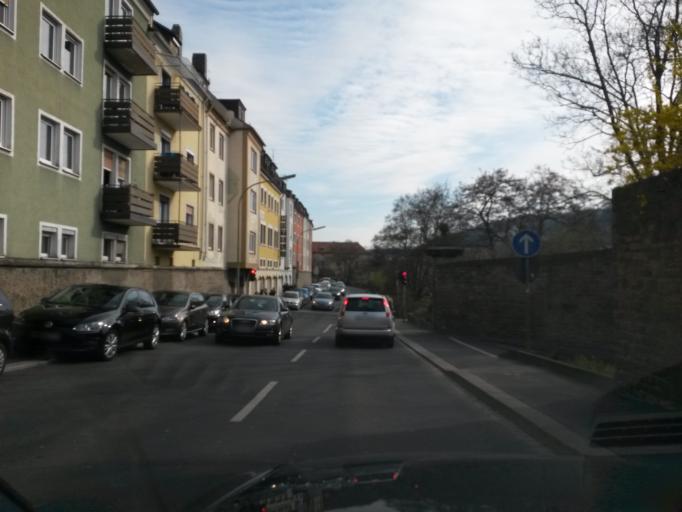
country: DE
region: Bavaria
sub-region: Regierungsbezirk Unterfranken
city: Wuerzburg
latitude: 49.7952
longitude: 9.9267
